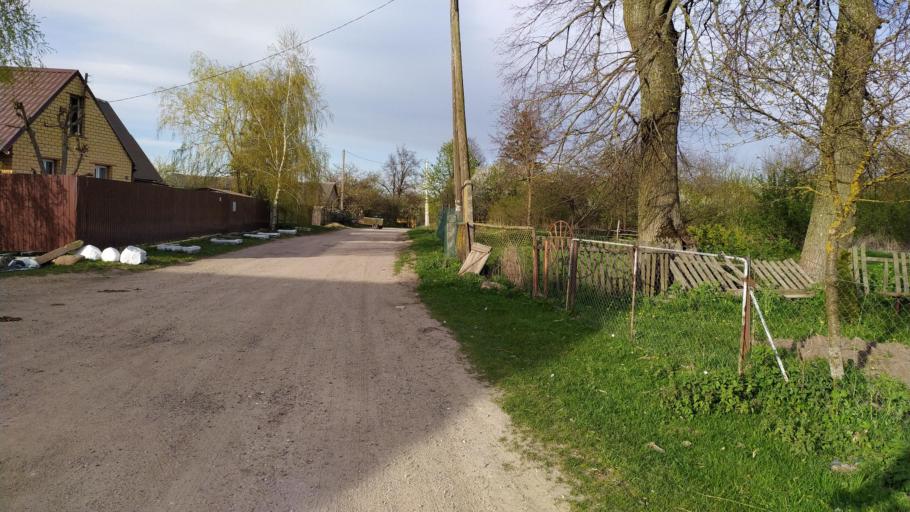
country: BY
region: Brest
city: Kamyanyets
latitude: 52.4078
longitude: 23.6640
